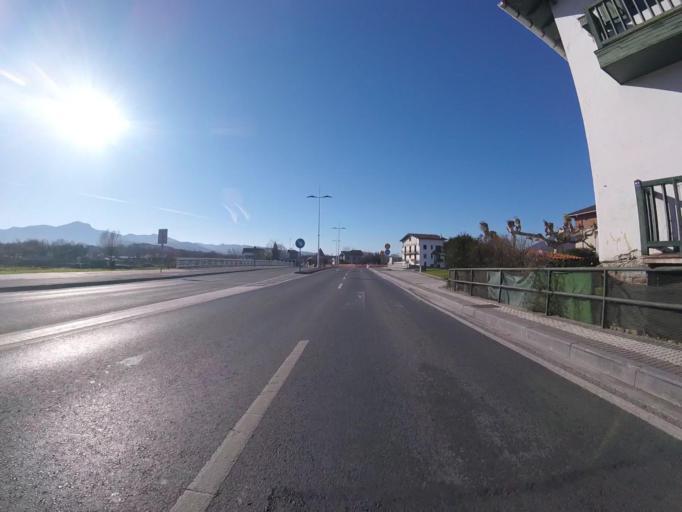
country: ES
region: Basque Country
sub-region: Provincia de Guipuzcoa
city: Irun
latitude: 43.3511
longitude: -1.7987
